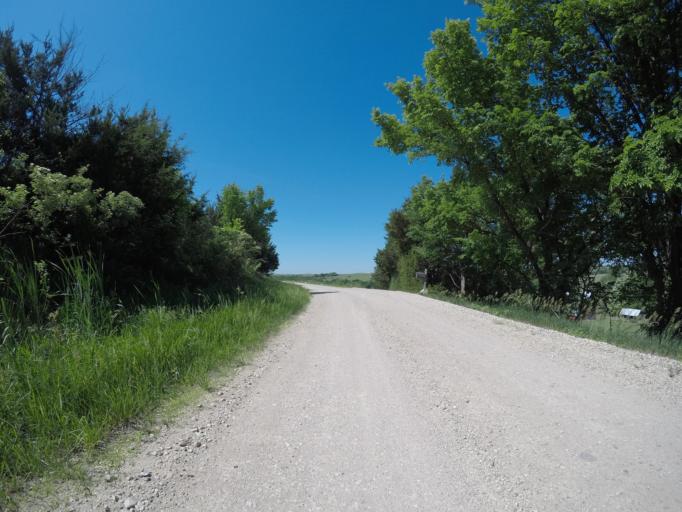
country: US
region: Kansas
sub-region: Wabaunsee County
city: Alma
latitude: 39.0176
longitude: -96.1525
